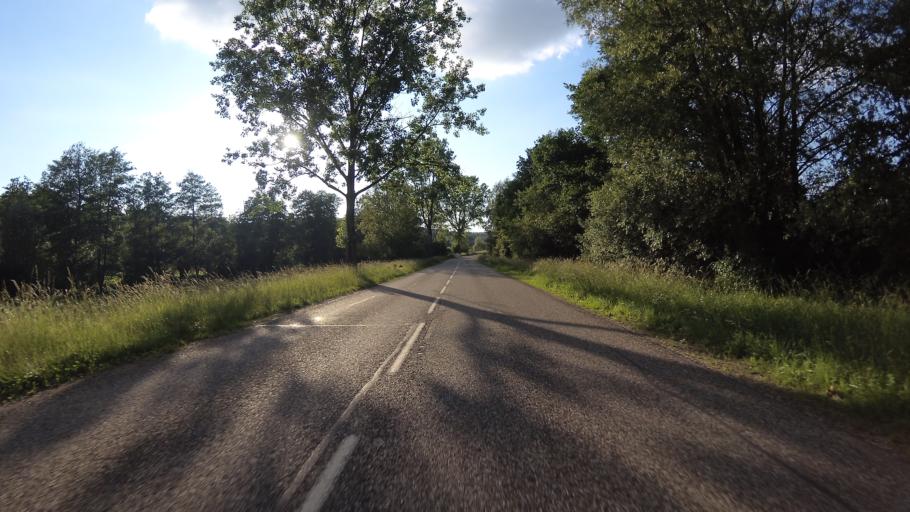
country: FR
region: Alsace
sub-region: Departement du Bas-Rhin
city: Oermingen
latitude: 48.9938
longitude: 7.1350
